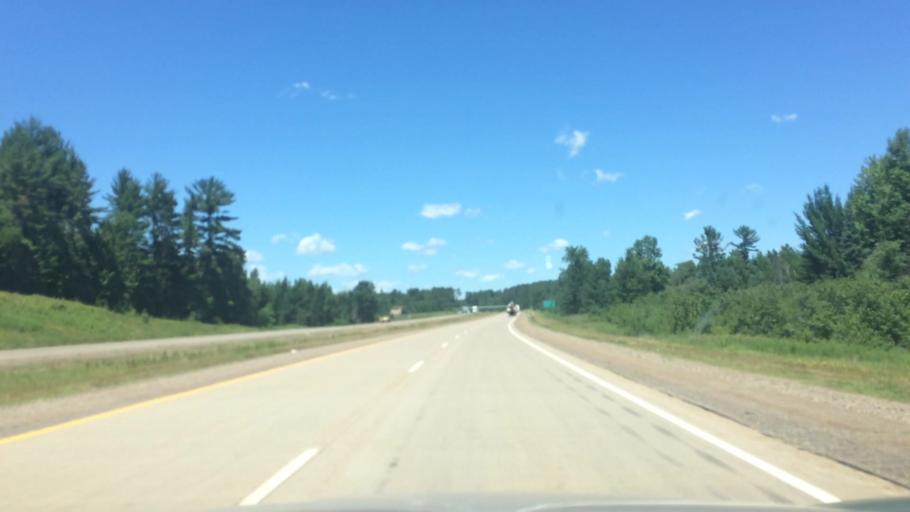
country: US
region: Wisconsin
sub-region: Lincoln County
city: Tomahawk
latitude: 45.4295
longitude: -89.6782
